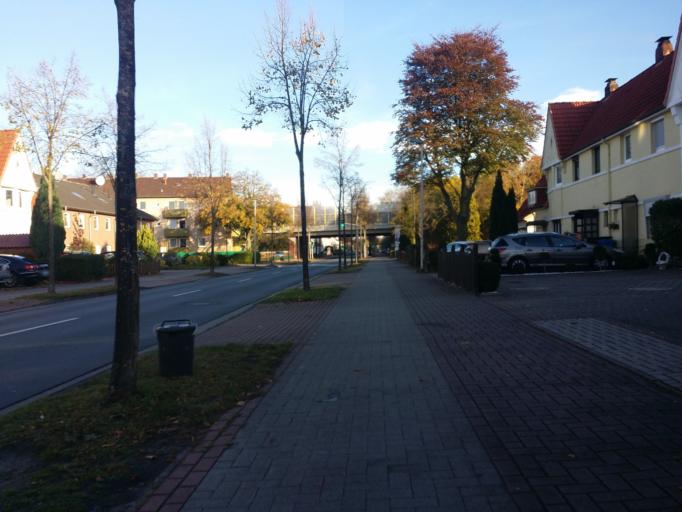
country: DE
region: Lower Saxony
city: Delmenhorst
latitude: 53.0312
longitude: 8.6393
